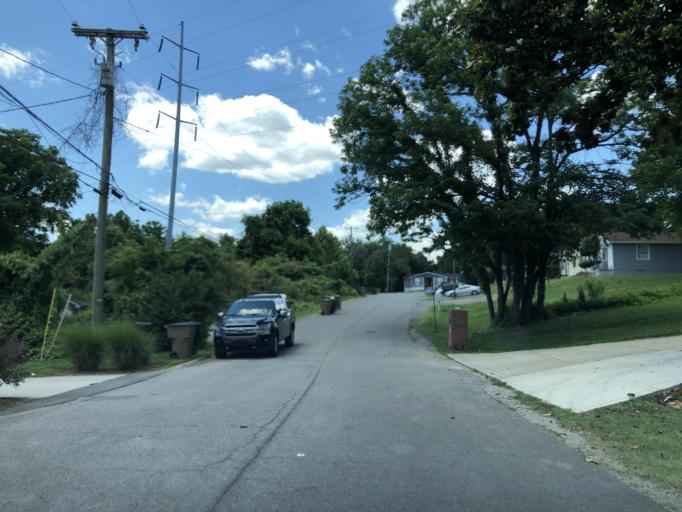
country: US
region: Tennessee
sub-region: Davidson County
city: Nashville
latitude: 36.1831
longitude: -86.7218
